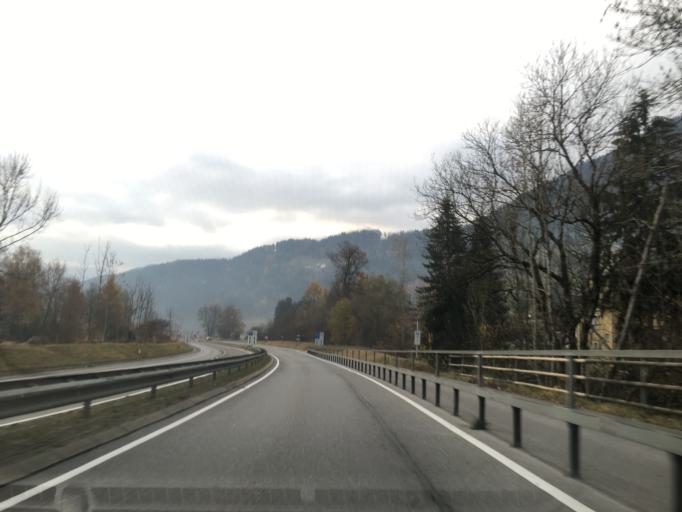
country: AT
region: Vorarlberg
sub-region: Politischer Bezirk Feldkirch
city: Feldkirch
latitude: 47.2276
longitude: 9.6044
